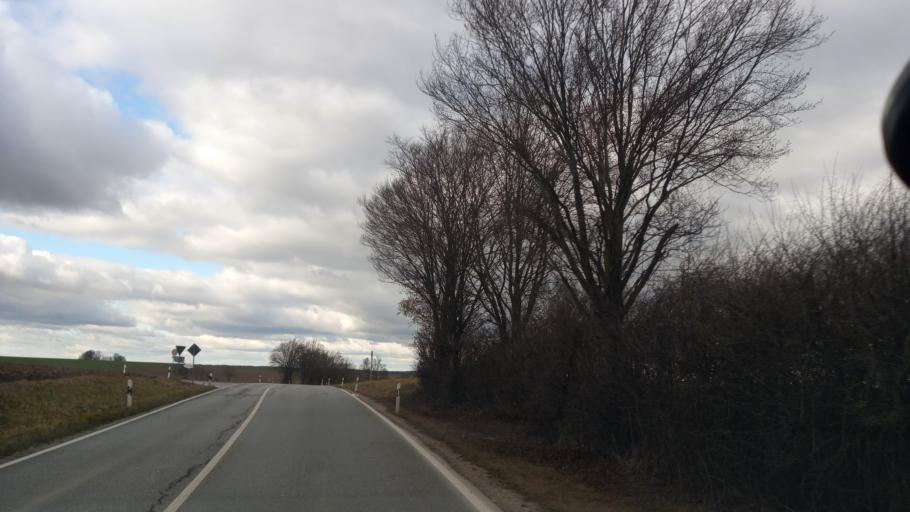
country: DE
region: Bavaria
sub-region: Upper Bavaria
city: Markt Indersdorf
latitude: 48.3287
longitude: 11.3882
